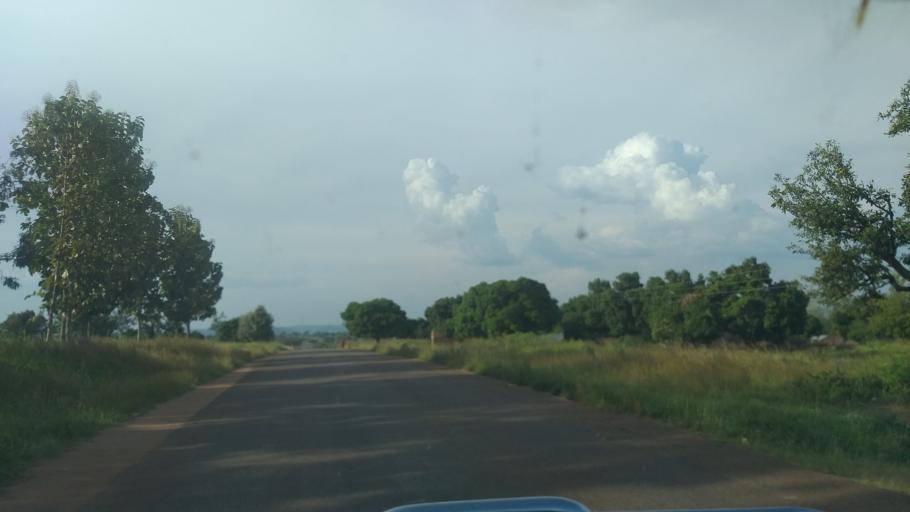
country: UG
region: Northern Region
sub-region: Arua District
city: Arua
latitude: 2.8418
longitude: 30.9916
